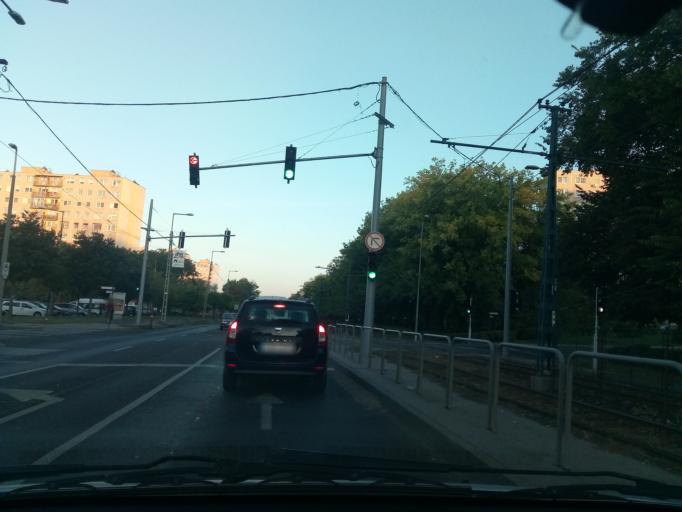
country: HU
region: Budapest
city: Budapest XIX. keruelet
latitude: 47.4551
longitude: 19.1506
